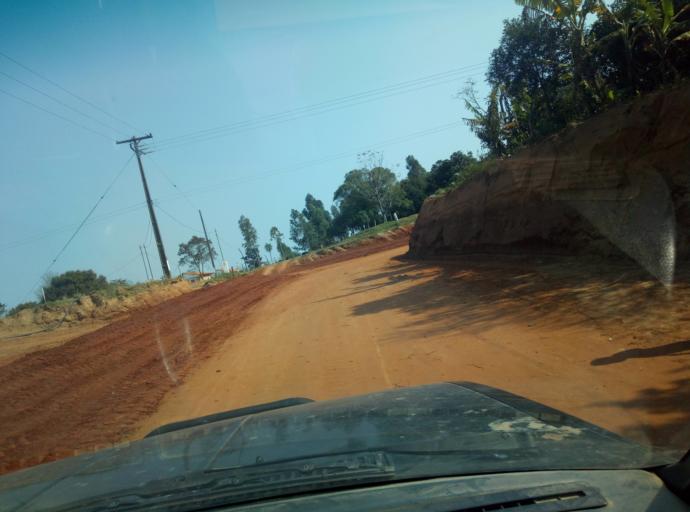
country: PY
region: Caaguazu
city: Coronel Oviedo
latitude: -25.3278
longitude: -56.3304
